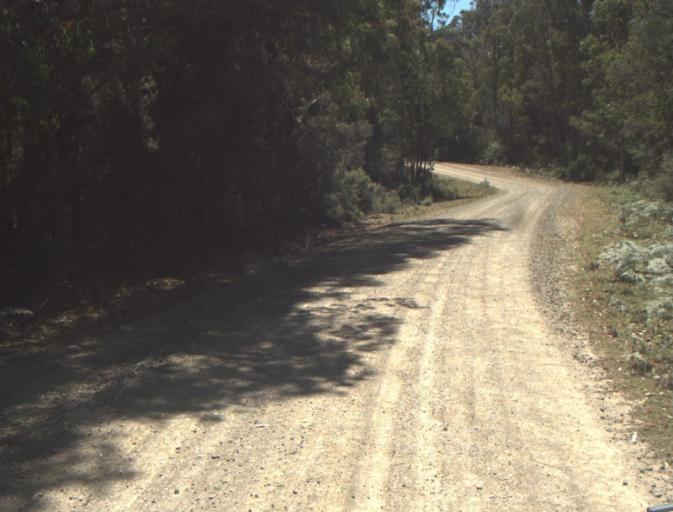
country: AU
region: Tasmania
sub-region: Dorset
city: Scottsdale
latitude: -41.3858
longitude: 147.5026
